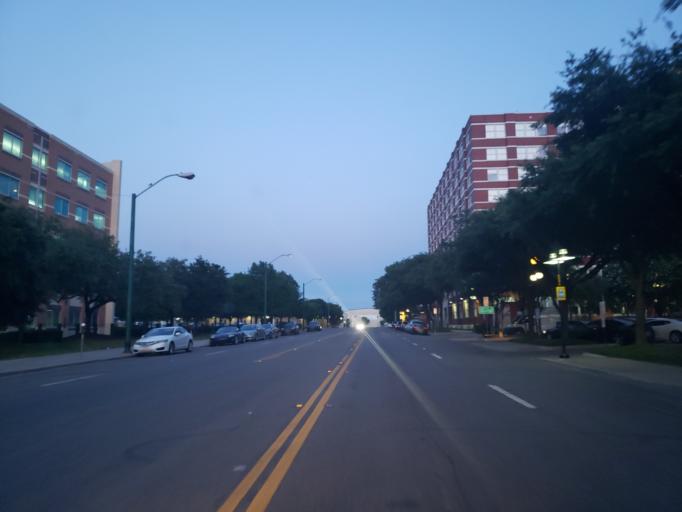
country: US
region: Texas
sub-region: Dallas County
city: Dallas
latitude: 32.7676
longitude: -96.7954
